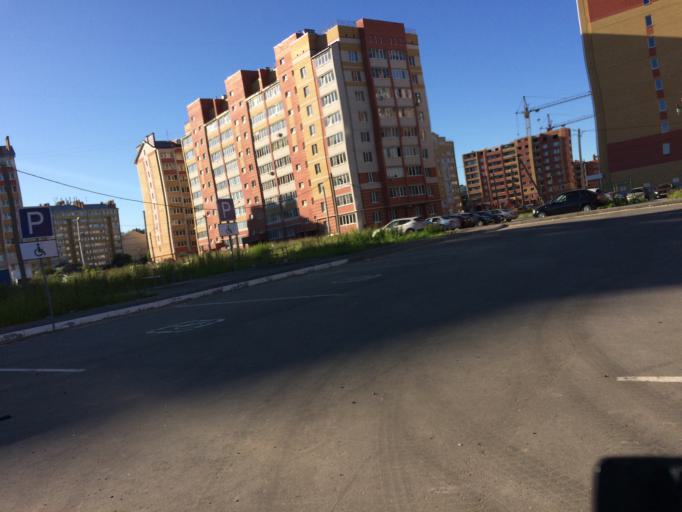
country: RU
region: Mariy-El
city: Medvedevo
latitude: 56.6477
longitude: 47.8326
